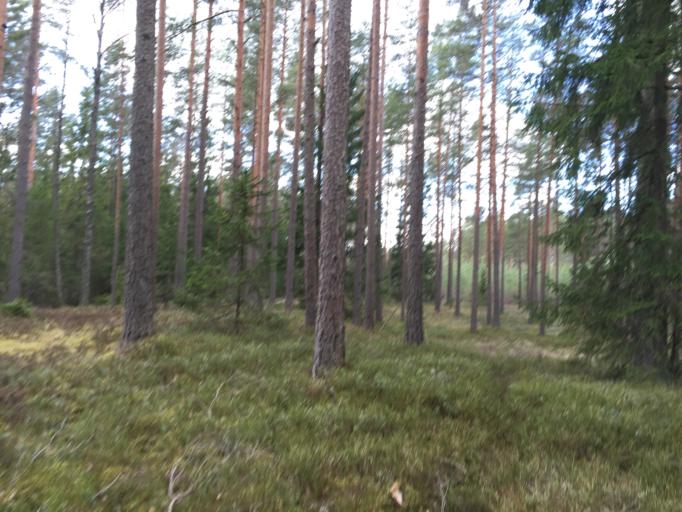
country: LV
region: Garkalne
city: Garkalne
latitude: 56.9607
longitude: 24.4926
